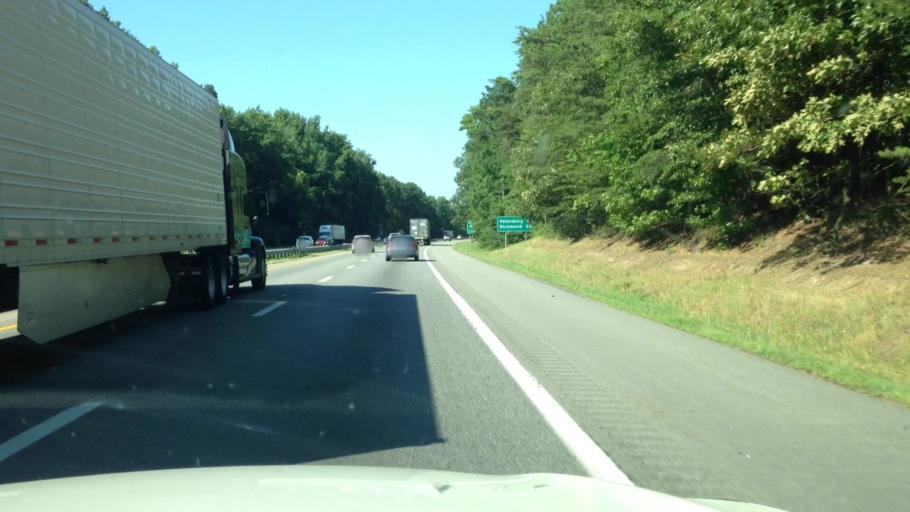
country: US
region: Virginia
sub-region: City of Emporia
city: Emporia
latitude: 36.7111
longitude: -77.5443
